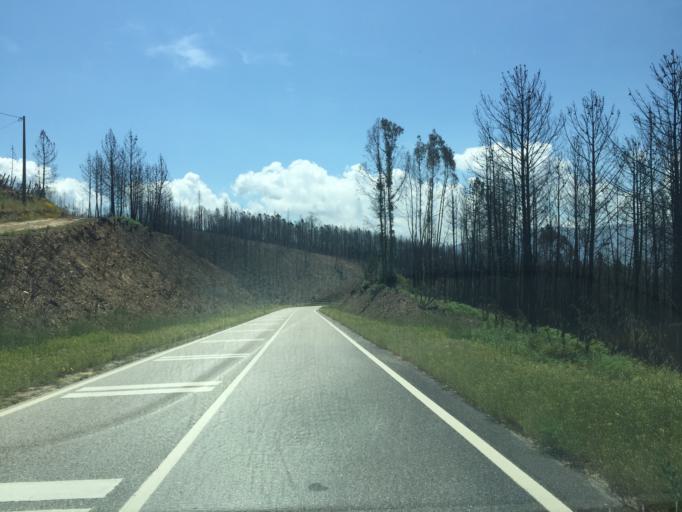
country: PT
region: Coimbra
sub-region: Pampilhosa da Serra
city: Pampilhosa da Serra
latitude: 40.0046
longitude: -7.9778
